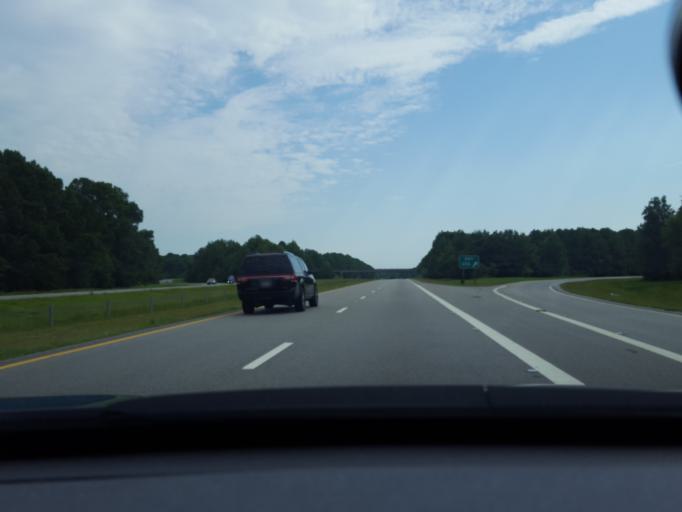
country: US
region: North Carolina
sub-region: Chowan County
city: Edenton
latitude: 36.0686
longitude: -76.6358
